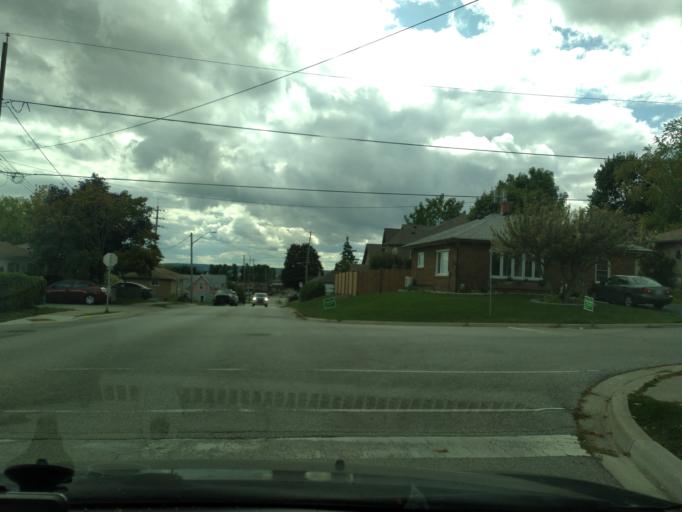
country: CA
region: Ontario
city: Bradford West Gwillimbury
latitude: 44.1173
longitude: -79.5613
